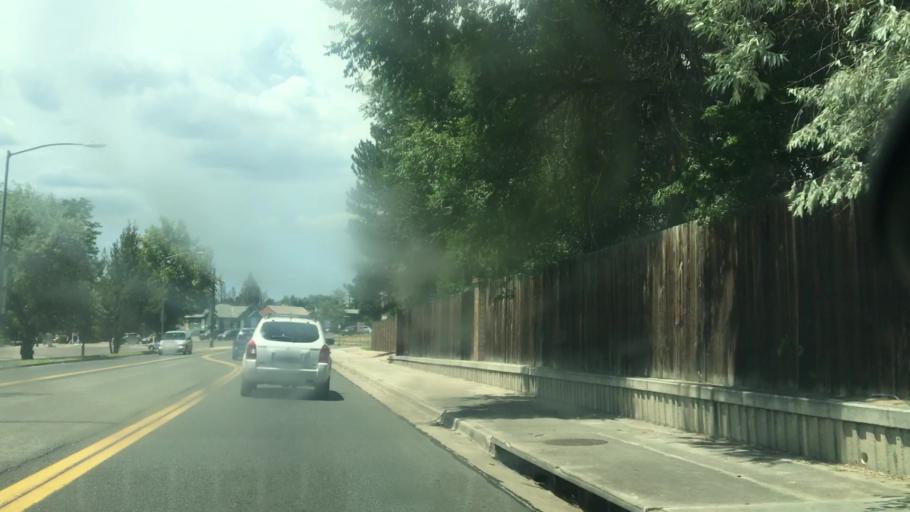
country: US
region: Colorado
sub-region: Arapahoe County
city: Glendale
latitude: 39.7141
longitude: -104.9395
